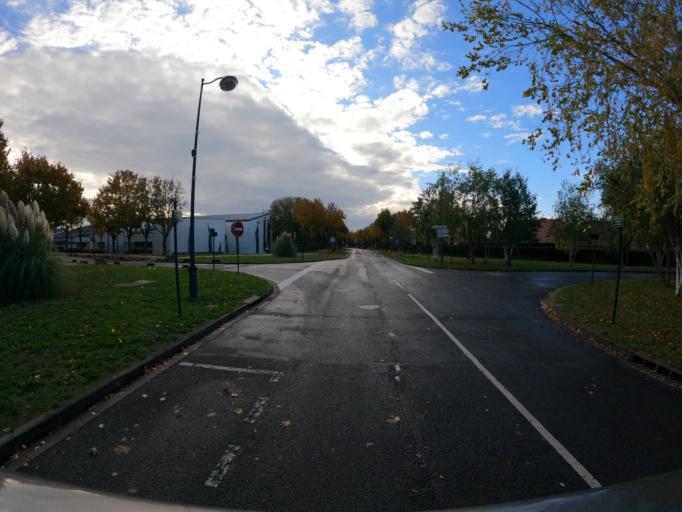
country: FR
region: Ile-de-France
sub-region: Departement de Seine-et-Marne
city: Bailly-Romainvilliers
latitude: 48.8461
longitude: 2.8163
